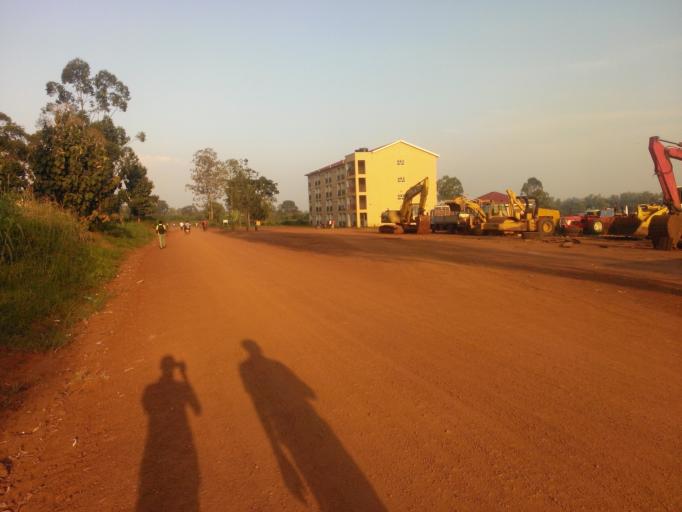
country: UG
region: Northern Region
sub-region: Gulu District
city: Gulu
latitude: 2.7795
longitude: 32.3050
